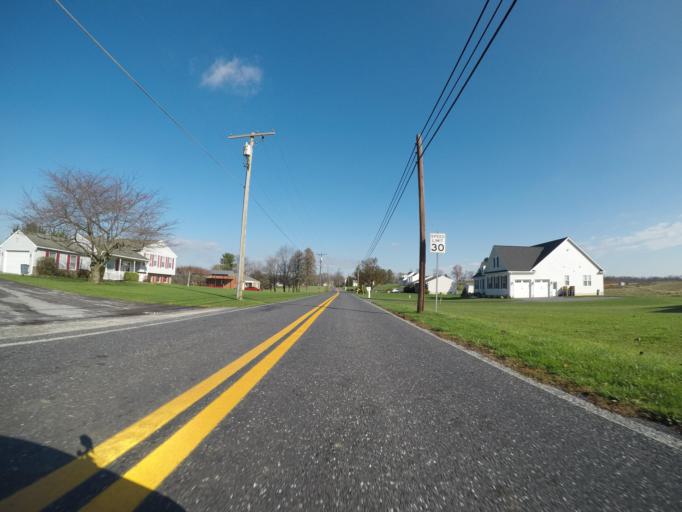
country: US
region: Maryland
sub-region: Carroll County
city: Hampstead
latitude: 39.5675
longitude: -76.8813
